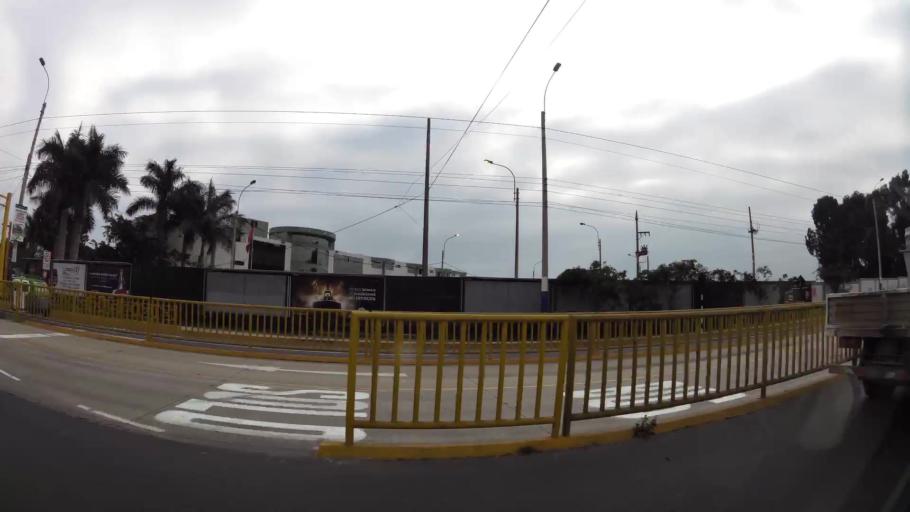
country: PE
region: Lima
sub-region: Lima
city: Surco
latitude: -12.1619
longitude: -77.0192
